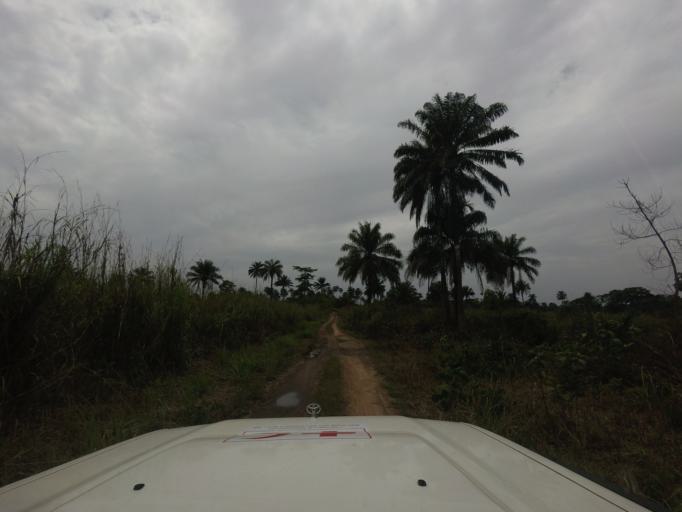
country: GN
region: Nzerekore
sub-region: Prefecture de Guekedou
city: Gueckedou
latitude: 8.4267
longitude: -10.2471
